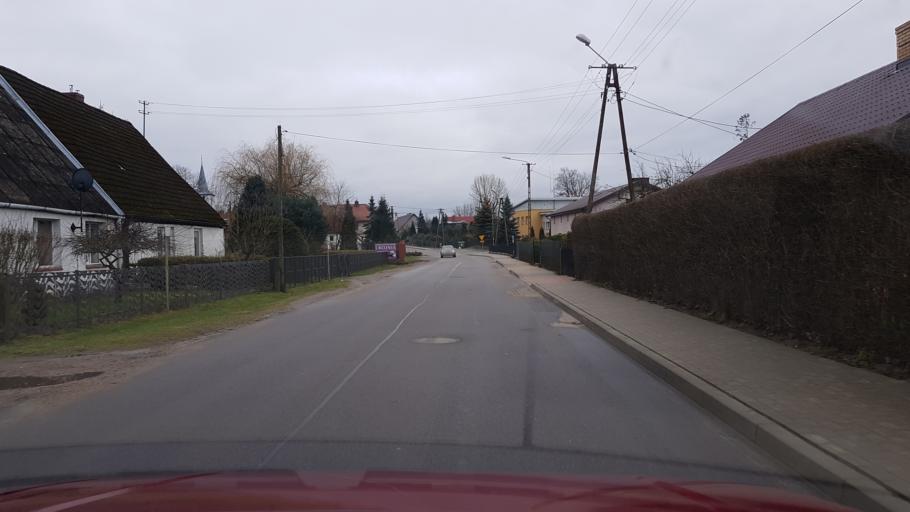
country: PL
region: West Pomeranian Voivodeship
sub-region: Powiat koszalinski
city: Mielno
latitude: 54.1351
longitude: 16.0374
